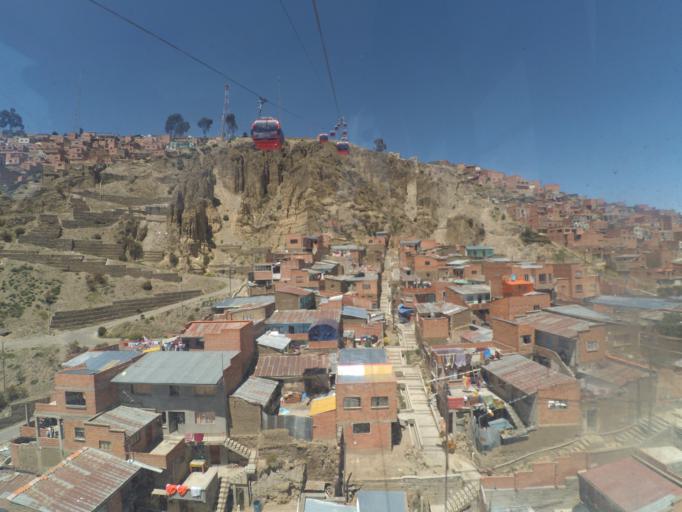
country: BO
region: La Paz
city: La Paz
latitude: -16.4977
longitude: -68.1603
